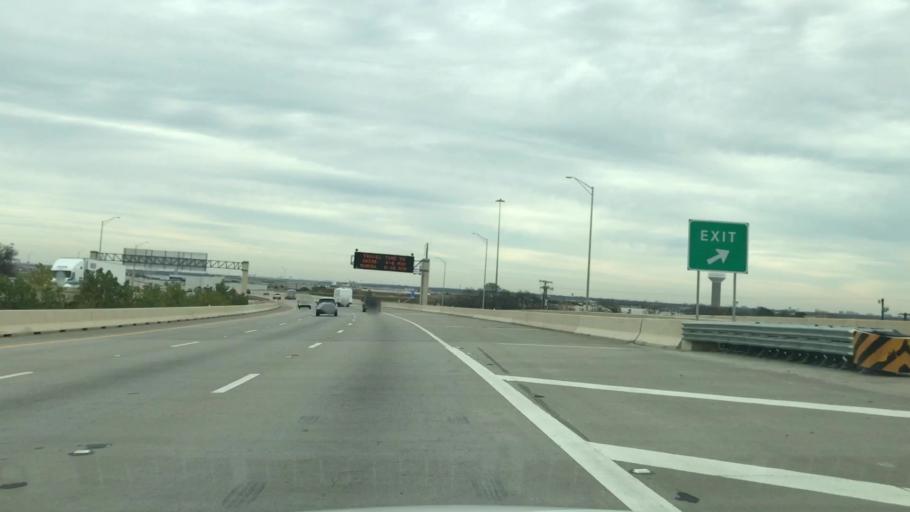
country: US
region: Texas
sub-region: Dallas County
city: Farmers Branch
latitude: 32.9160
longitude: -96.9350
